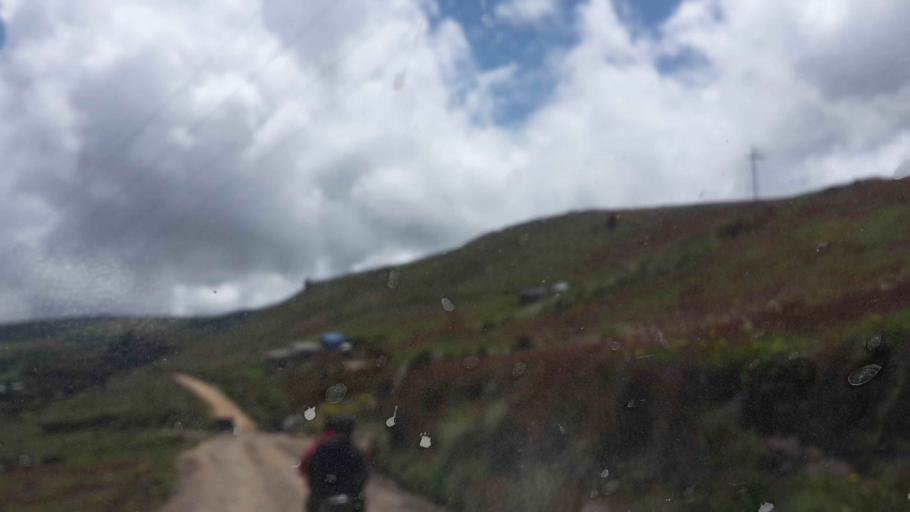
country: BO
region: Cochabamba
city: Cochabamba
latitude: -17.1887
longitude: -66.0755
